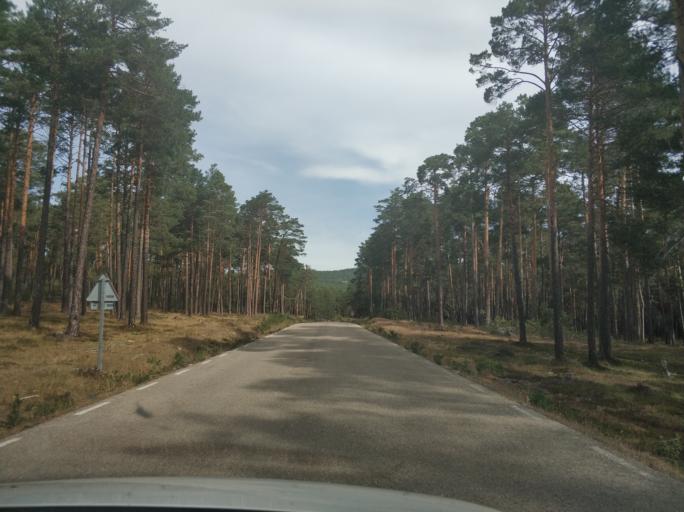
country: ES
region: Castille and Leon
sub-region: Provincia de Soria
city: Navaleno
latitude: 41.8737
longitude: -2.9385
